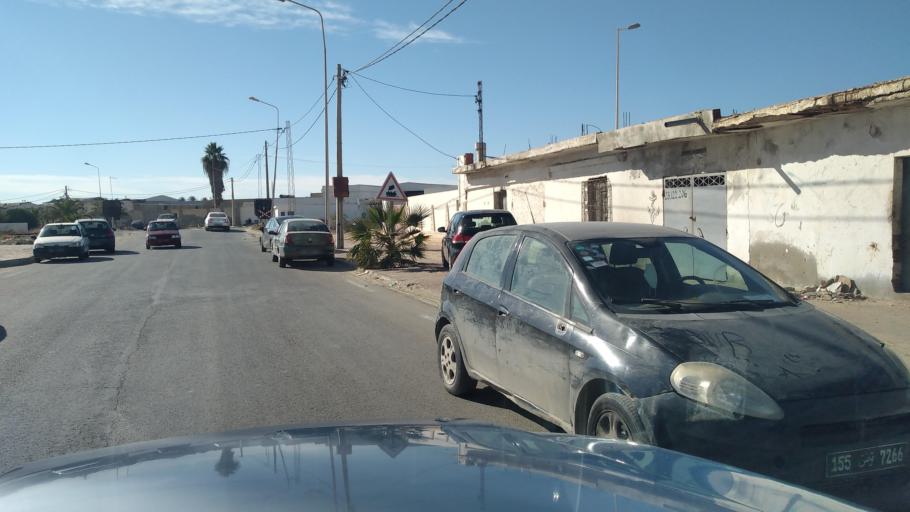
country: TN
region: Qabis
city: Gabes
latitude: 33.8933
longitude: 10.1121
